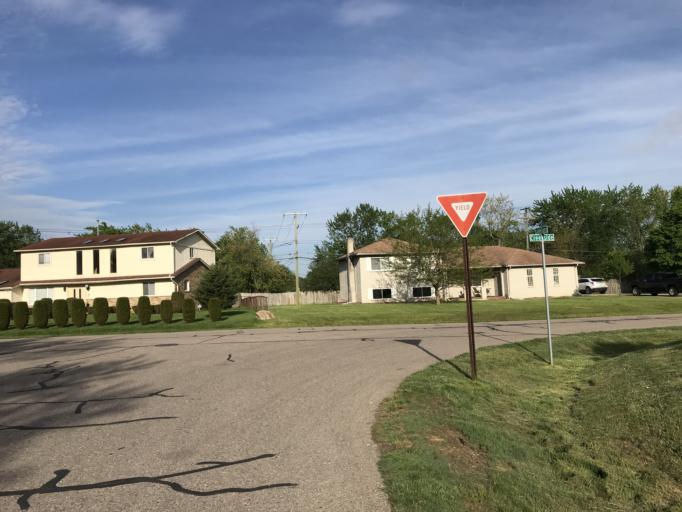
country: US
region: Michigan
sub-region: Oakland County
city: Farmington Hills
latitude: 42.4773
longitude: -83.3438
